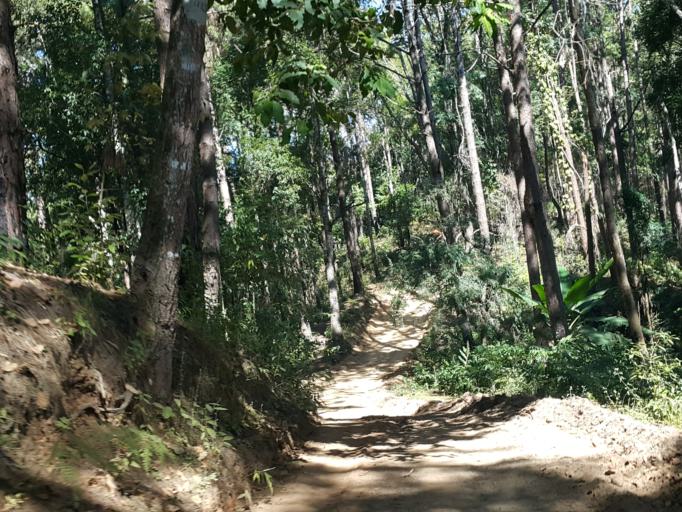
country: TH
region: Chiang Mai
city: Wiang Haeng
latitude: 19.5256
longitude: 98.8095
